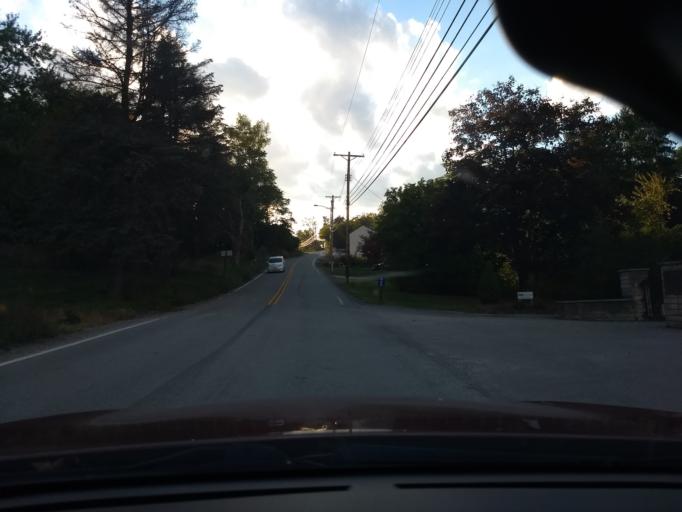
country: US
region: Pennsylvania
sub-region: Allegheny County
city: Dravosburg
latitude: 40.3594
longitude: -79.8850
